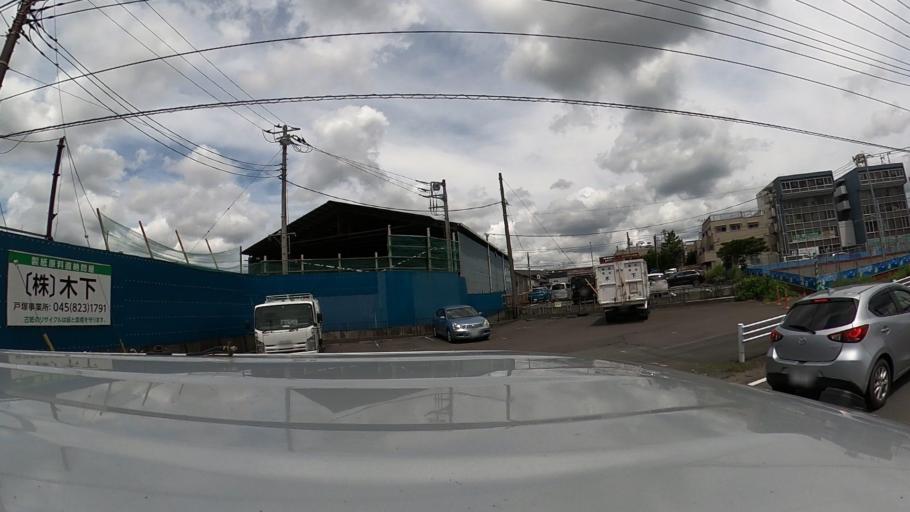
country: JP
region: Kanagawa
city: Fujisawa
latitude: 35.4139
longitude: 139.5418
